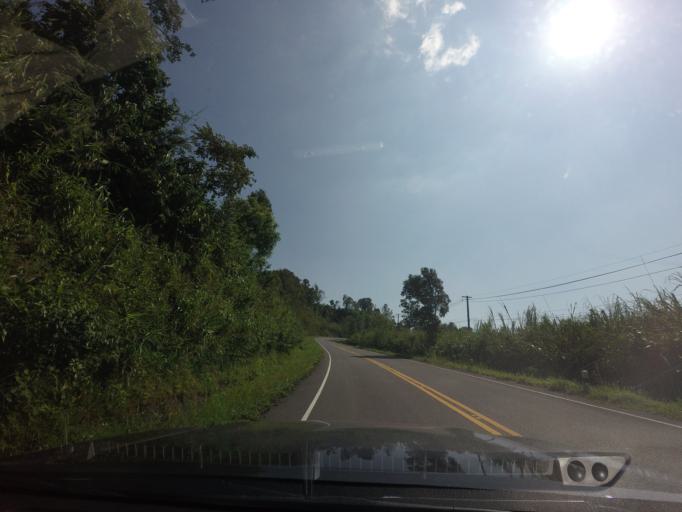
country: TH
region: Nan
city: Bo Kluea
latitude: 19.0482
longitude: 101.0907
